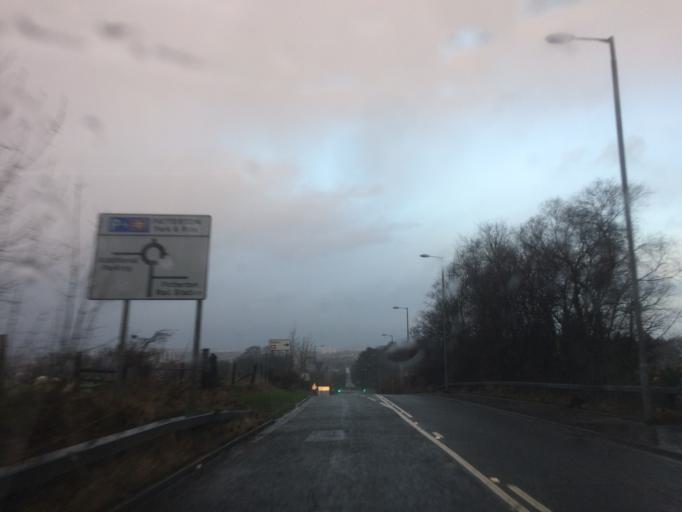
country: GB
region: Scotland
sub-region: East Renfrewshire
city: Newton Mearns
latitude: 55.7900
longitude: -4.3374
